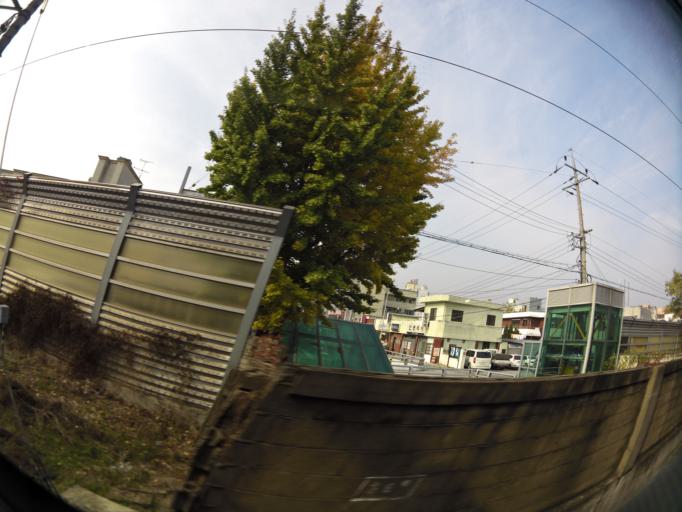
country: KR
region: Gyeongsangbuk-do
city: Waegwan
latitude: 35.9963
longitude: 128.4003
